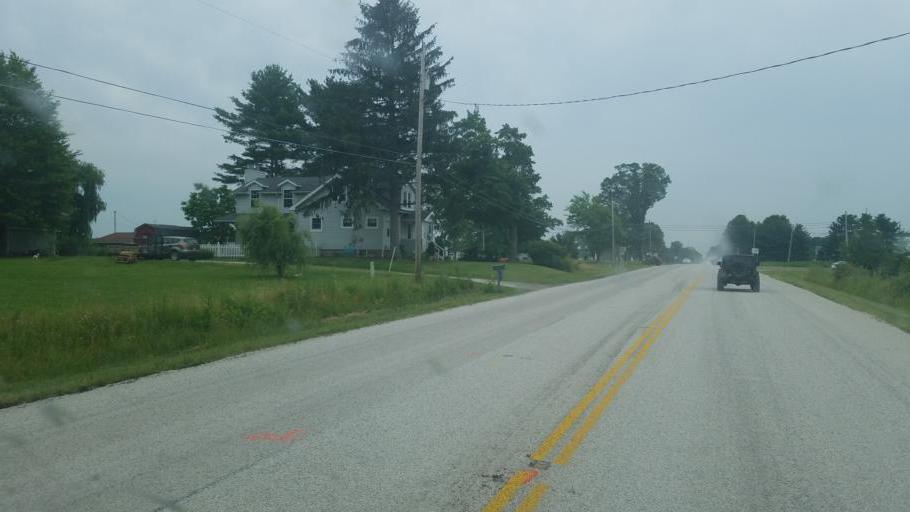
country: US
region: Ohio
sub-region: Mahoning County
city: Craig Beach
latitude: 41.1353
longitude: -81.0512
